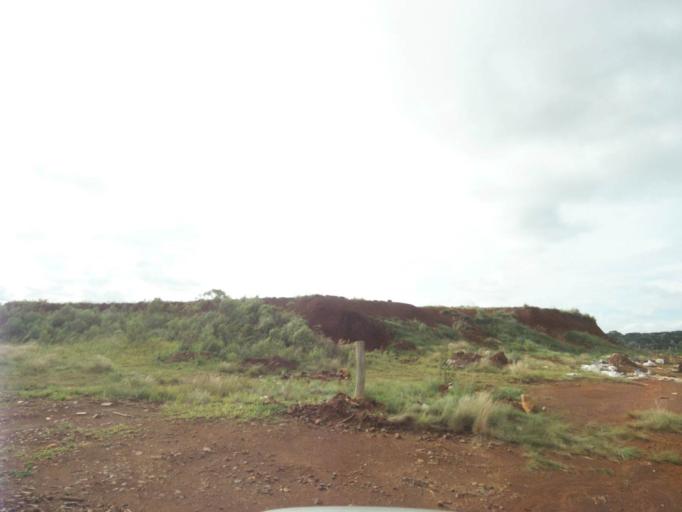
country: BR
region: Rio Grande do Sul
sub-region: Lagoa Vermelha
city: Lagoa Vermelha
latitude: -28.2032
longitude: -51.5327
